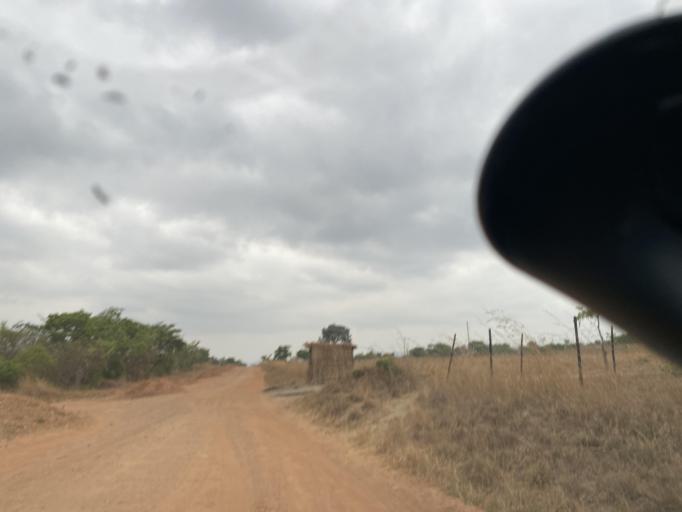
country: ZM
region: Lusaka
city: Chongwe
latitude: -15.2587
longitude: 28.7311
